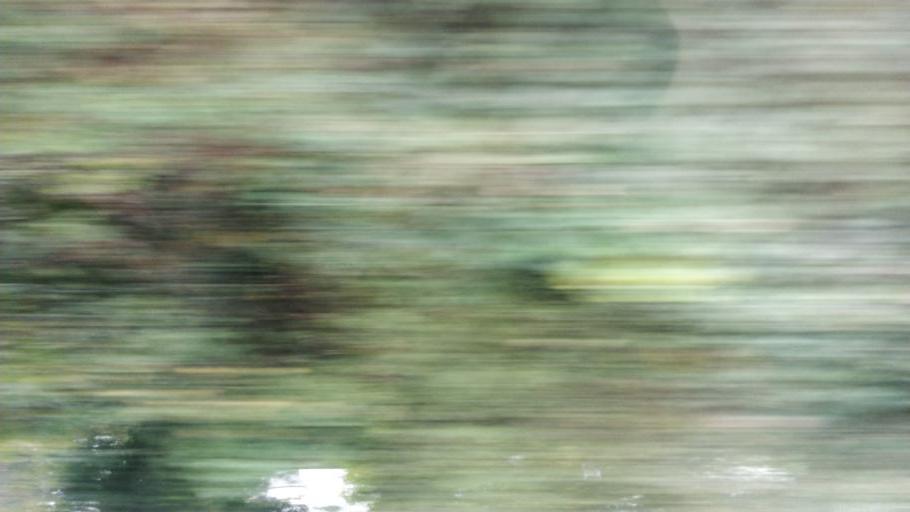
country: GB
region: England
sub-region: Borough of Wigan
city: Tyldesley
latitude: 53.5288
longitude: -2.4741
